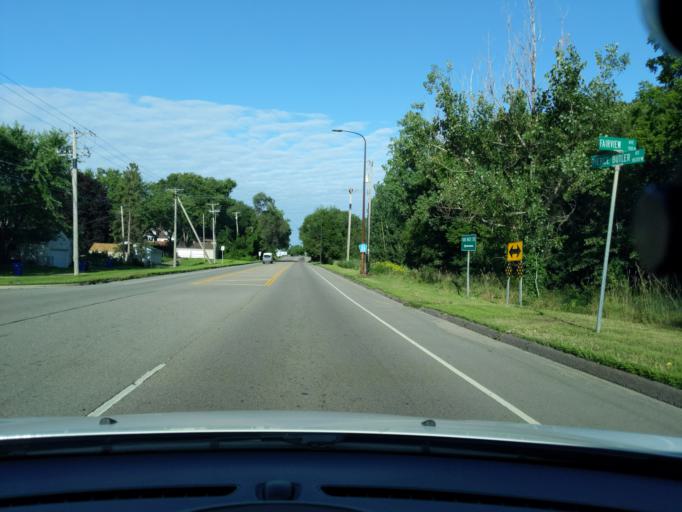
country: US
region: Minnesota
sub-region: Ramsey County
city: Falcon Heights
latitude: 44.9688
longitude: -93.1770
